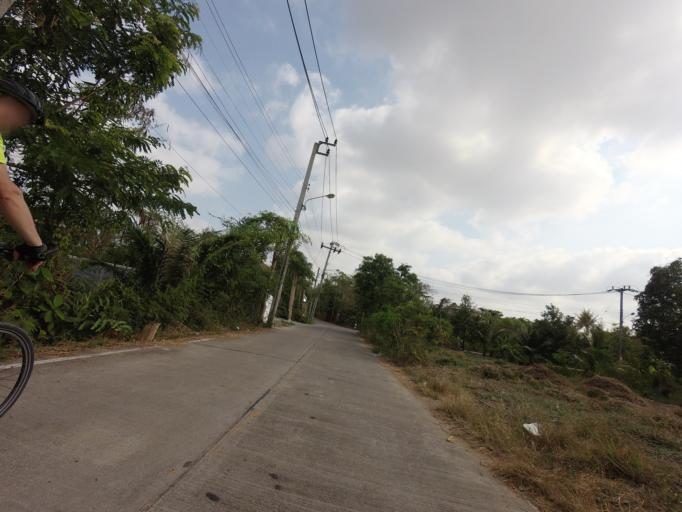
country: TH
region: Bangkok
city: Khlong Toei
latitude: 13.6999
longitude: 100.5668
